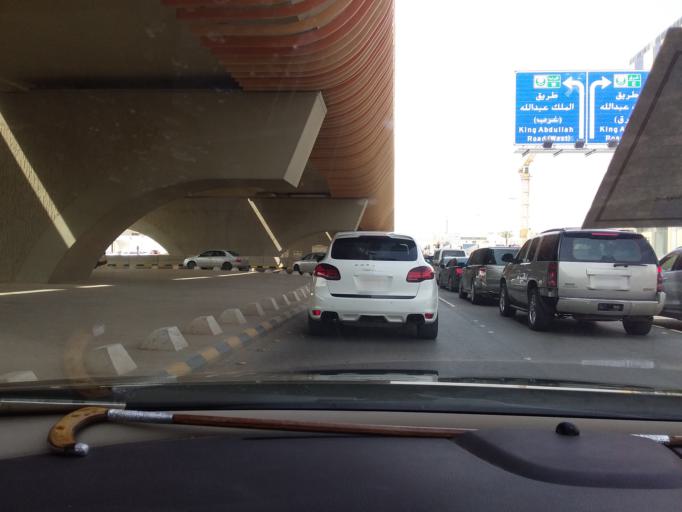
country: SA
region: Ar Riyad
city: Riyadh
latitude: 24.7432
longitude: 46.7038
